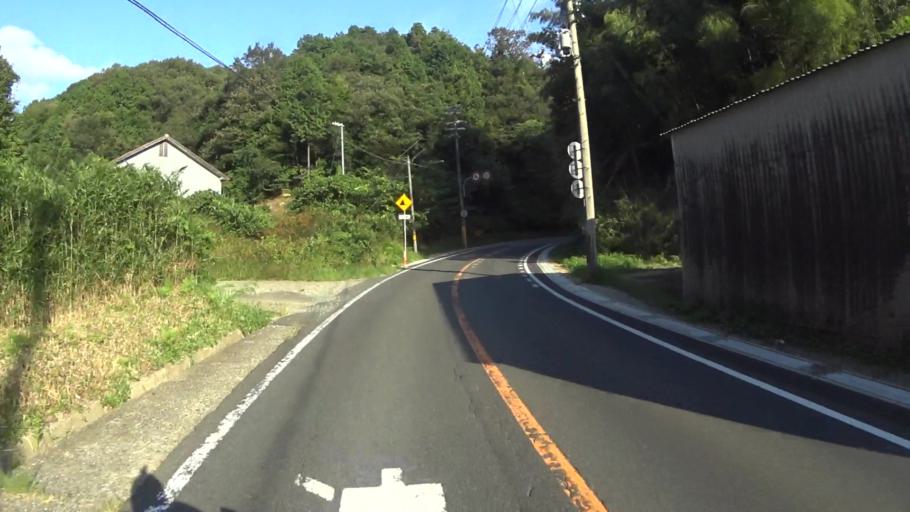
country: JP
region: Hyogo
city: Toyooka
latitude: 35.5941
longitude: 134.9121
